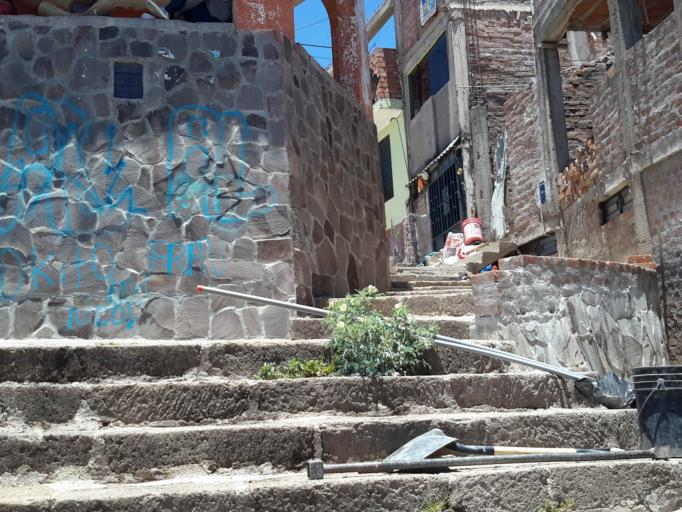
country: PE
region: Ayacucho
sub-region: Provincia de Huamanga
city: Carmen Alto
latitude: -13.1707
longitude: -74.2226
